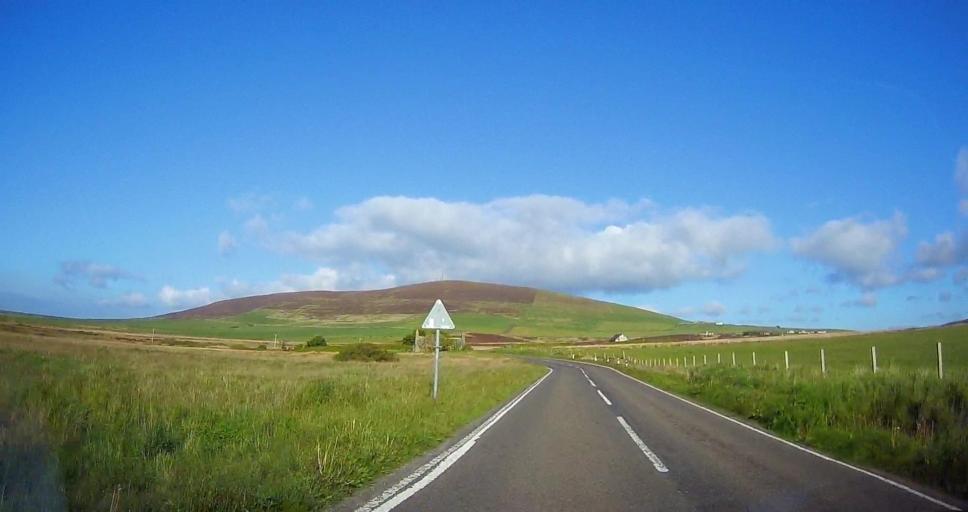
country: GB
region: Scotland
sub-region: Orkney Islands
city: Orkney
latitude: 58.9886
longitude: -3.0601
